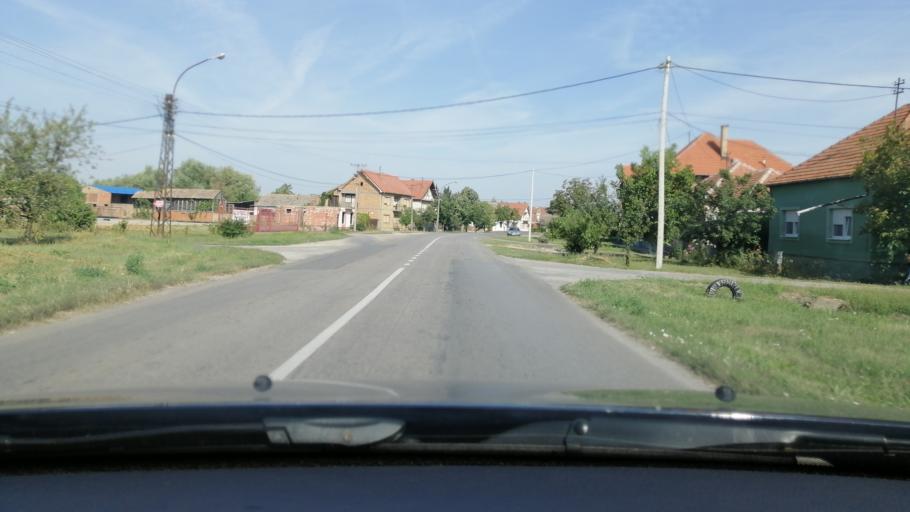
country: RS
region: Autonomna Pokrajina Vojvodina
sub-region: Juznobanatski Okrug
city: Kovacica
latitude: 45.1062
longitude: 20.6204
